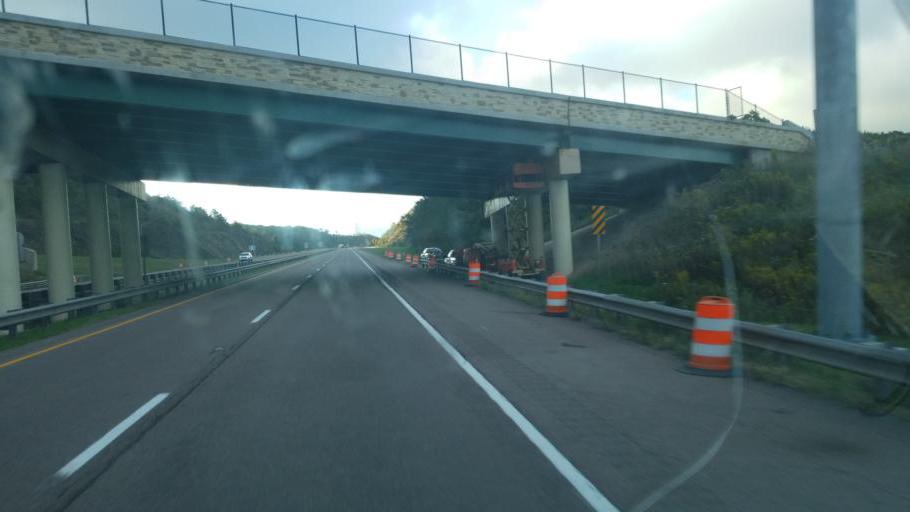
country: US
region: Maryland
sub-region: Allegany County
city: Frostburg
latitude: 39.6838
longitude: -78.9706
